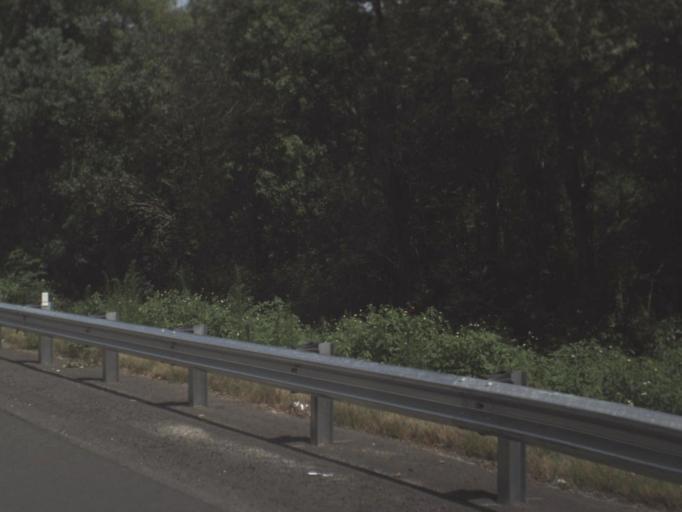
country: US
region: Florida
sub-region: Madison County
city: Madison
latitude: 30.4713
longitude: -83.6373
